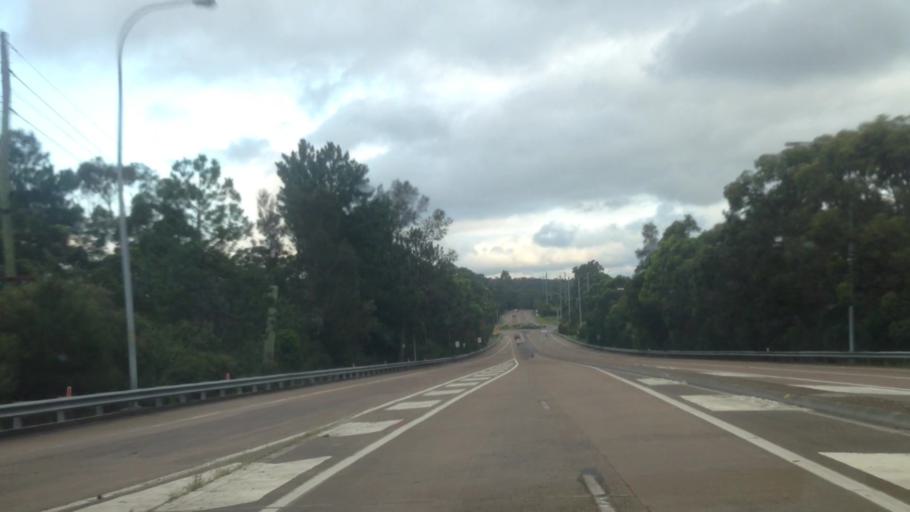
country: AU
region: New South Wales
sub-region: Lake Macquarie Shire
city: Cooranbong
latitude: -33.1179
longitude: 151.4668
